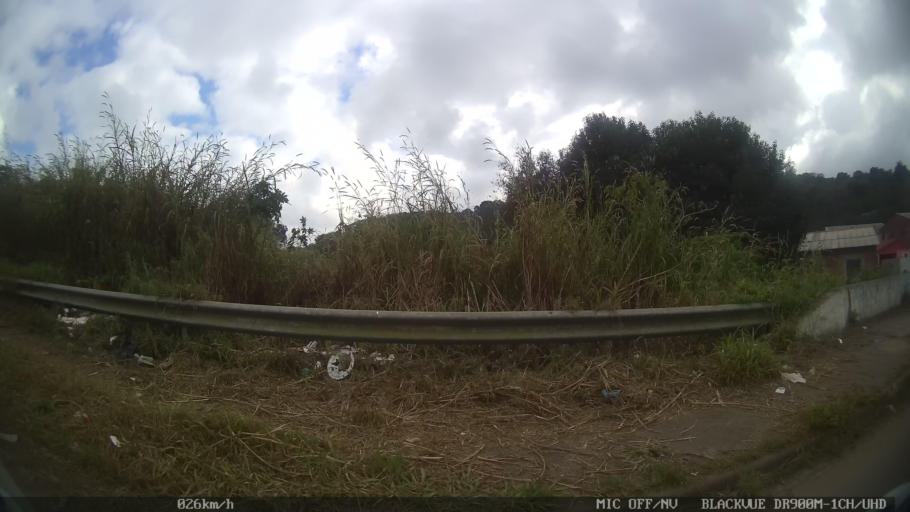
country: BR
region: Parana
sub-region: Colombo
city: Colombo
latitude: -25.3447
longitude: -49.2321
